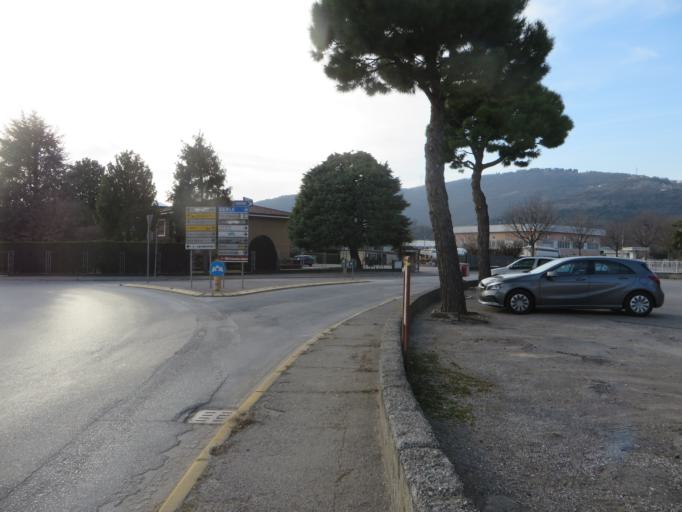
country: IT
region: Lombardy
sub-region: Provincia di Brescia
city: Nuvolento
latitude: 45.5481
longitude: 10.3944
